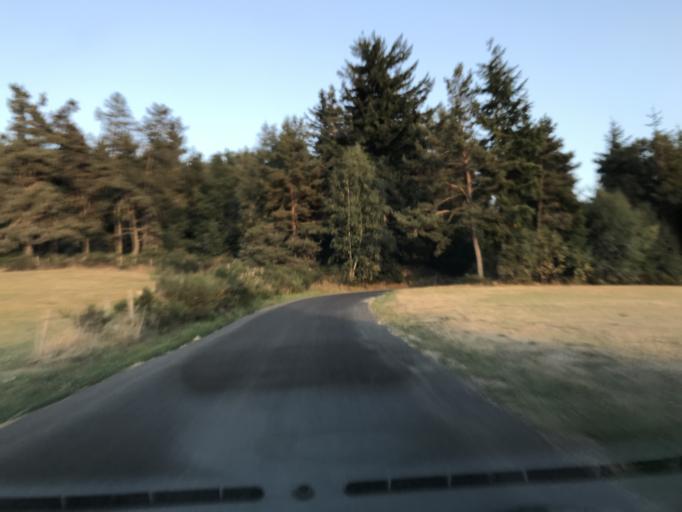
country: FR
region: Rhone-Alpes
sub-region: Departement de l'Ardeche
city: Saint-Agreve
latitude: 45.0140
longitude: 4.3920
